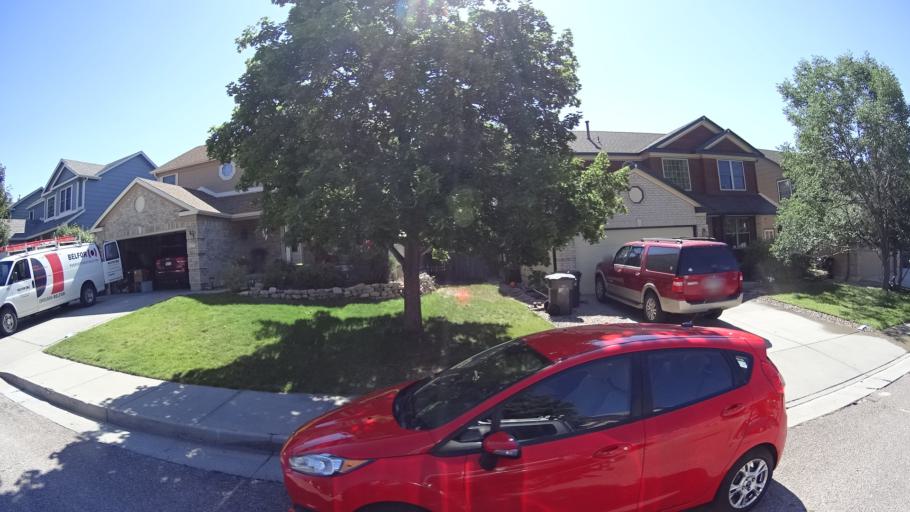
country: US
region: Colorado
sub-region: El Paso County
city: Black Forest
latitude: 38.9460
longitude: -104.7318
